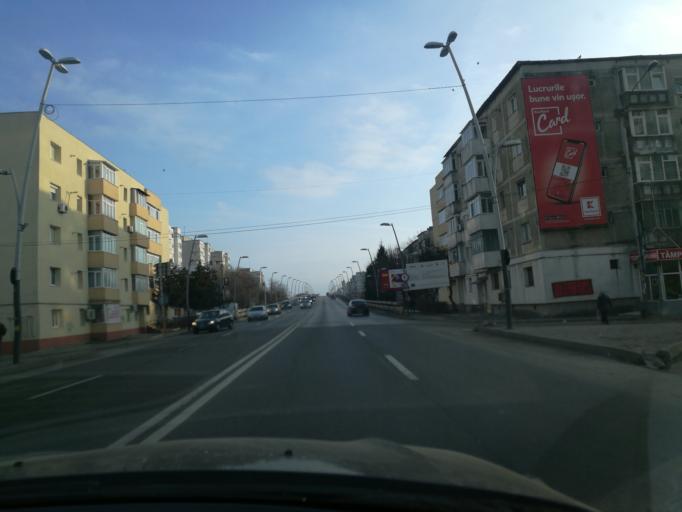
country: RO
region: Bacau
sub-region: Municipiul Bacau
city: Bacau
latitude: 46.5474
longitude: 26.9147
